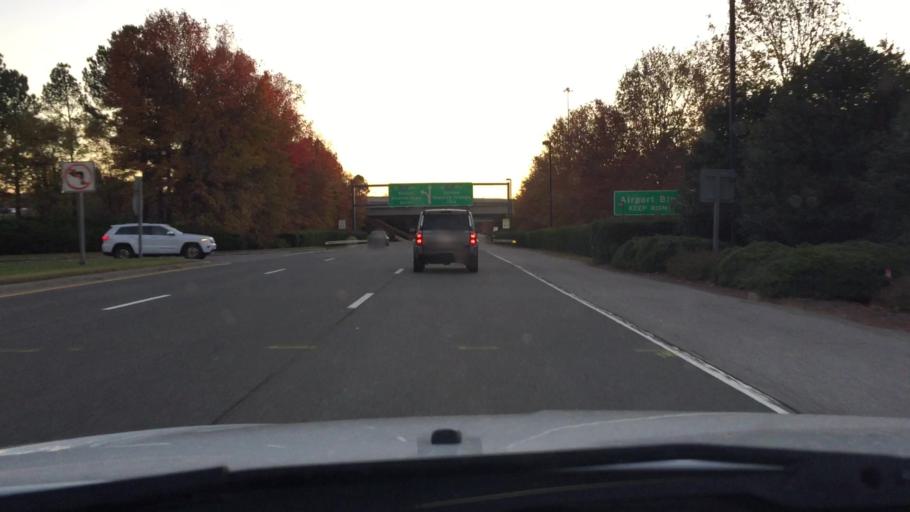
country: US
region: North Carolina
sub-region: Wake County
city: Morrisville
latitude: 35.8688
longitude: -78.8026
